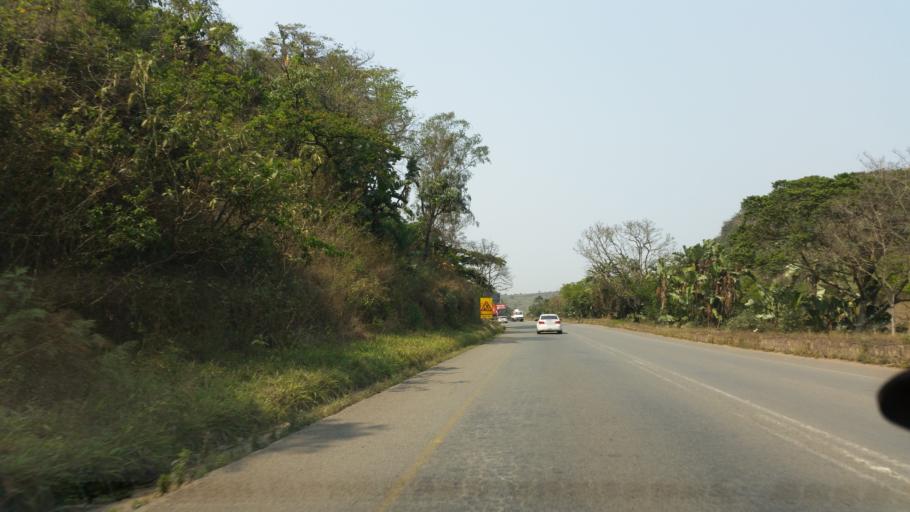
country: ZA
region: KwaZulu-Natal
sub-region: eThekwini Metropolitan Municipality
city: Mpumalanga
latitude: -29.7474
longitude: 30.6645
